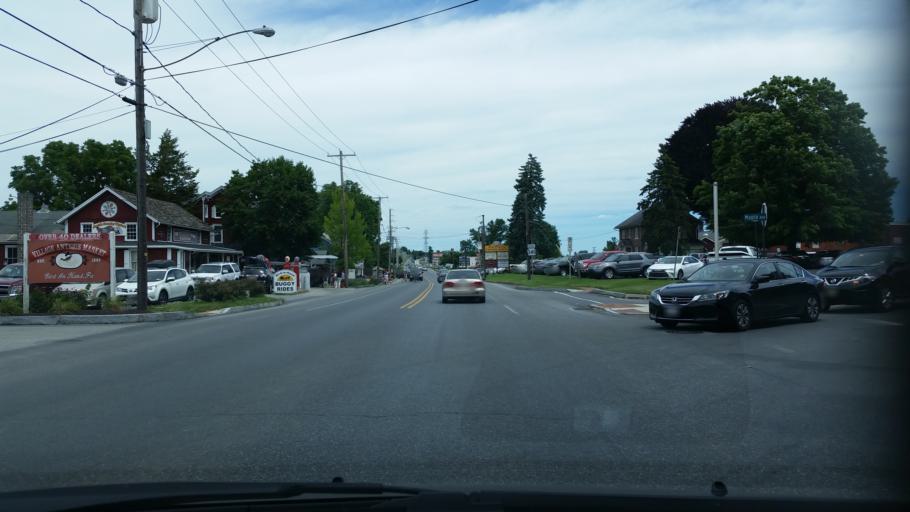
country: US
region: Pennsylvania
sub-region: Lancaster County
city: Strasburg
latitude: 40.0385
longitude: -76.1797
